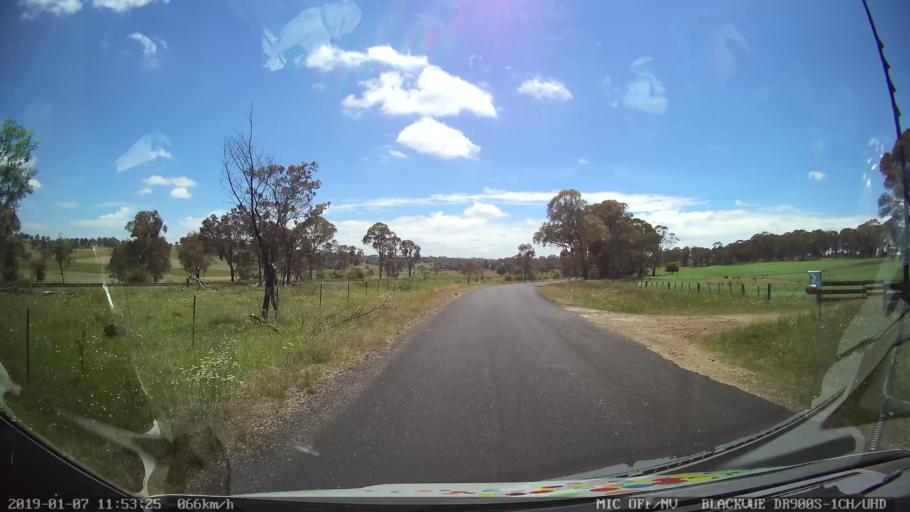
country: AU
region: New South Wales
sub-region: Guyra
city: Guyra
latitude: -30.3042
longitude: 151.6573
